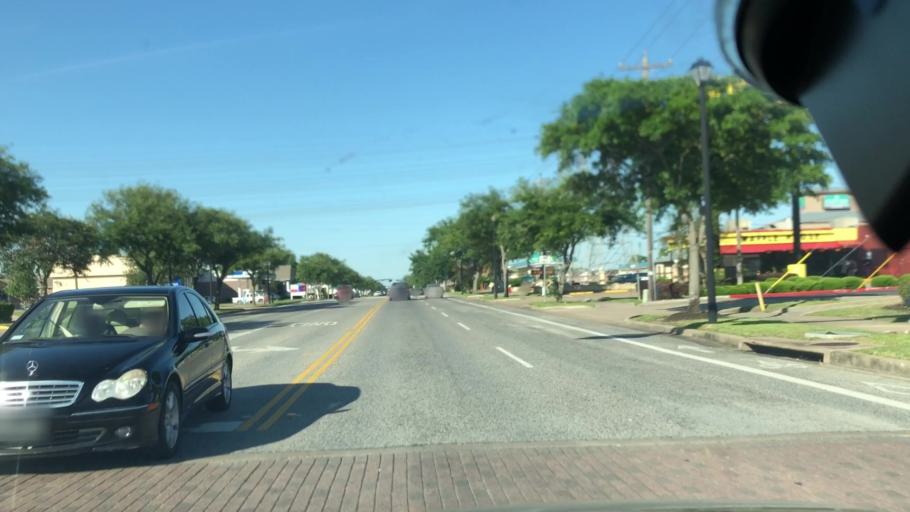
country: US
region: Texas
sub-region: Harris County
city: Webster
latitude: 29.5310
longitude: -95.1273
